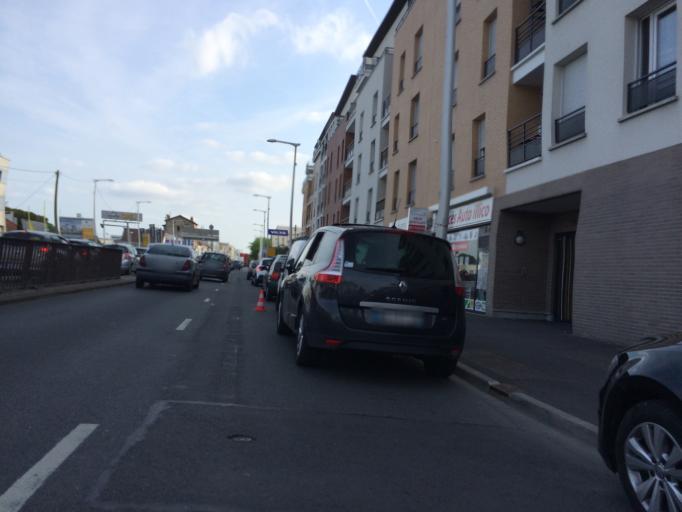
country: FR
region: Ile-de-France
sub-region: Departement de l'Essonne
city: Paray-Vieille-Poste
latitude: 48.7047
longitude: 2.3715
